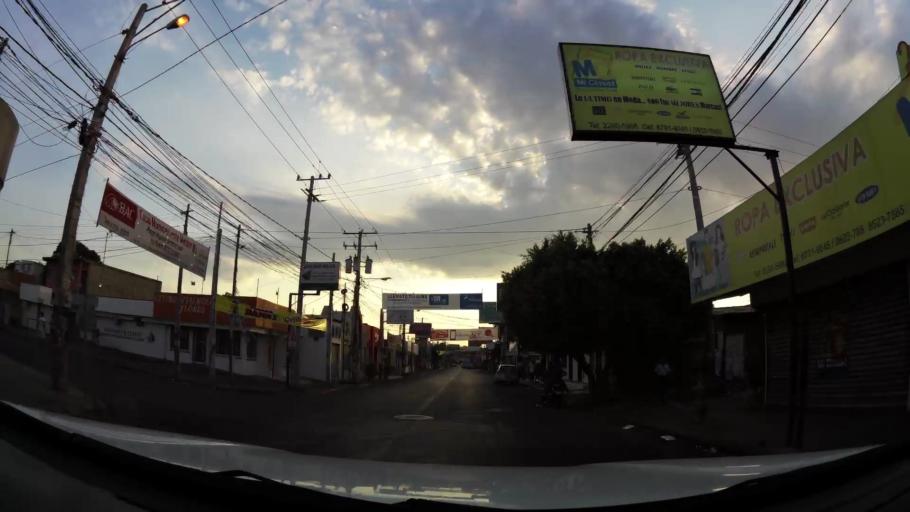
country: NI
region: Managua
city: Managua
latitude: 12.1446
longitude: -86.2550
